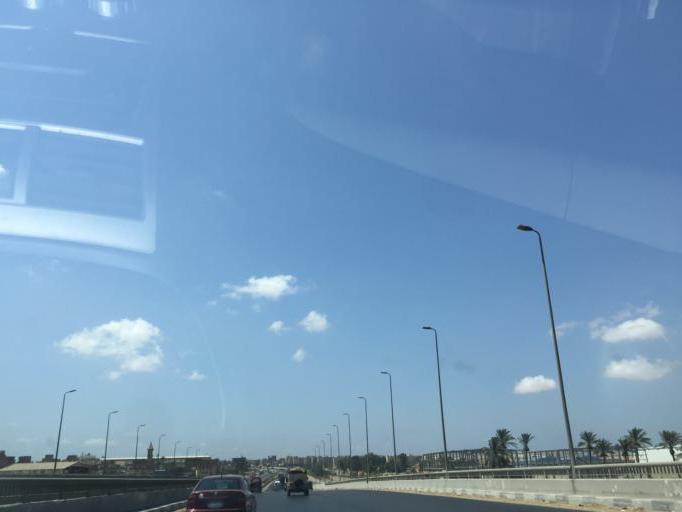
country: EG
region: Alexandria
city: Alexandria
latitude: 31.0175
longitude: 29.7953
